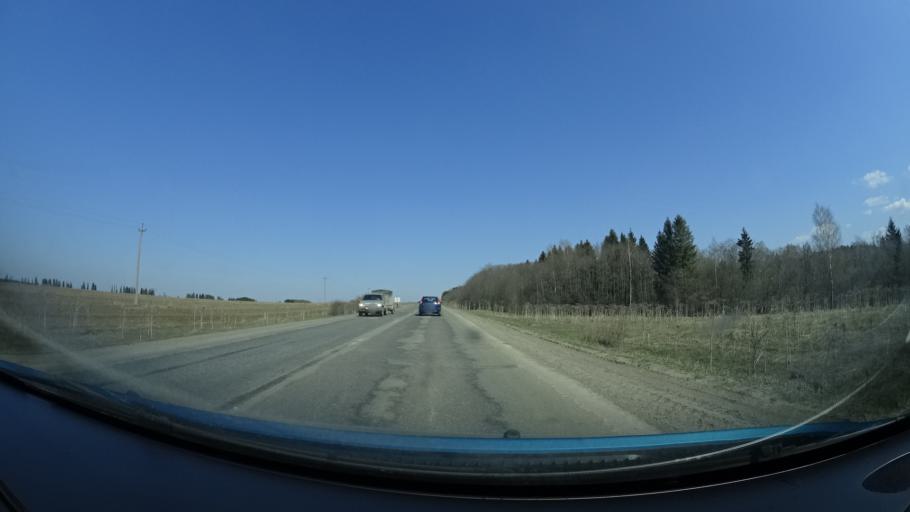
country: RU
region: Perm
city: Kultayevo
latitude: 57.8550
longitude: 55.8566
